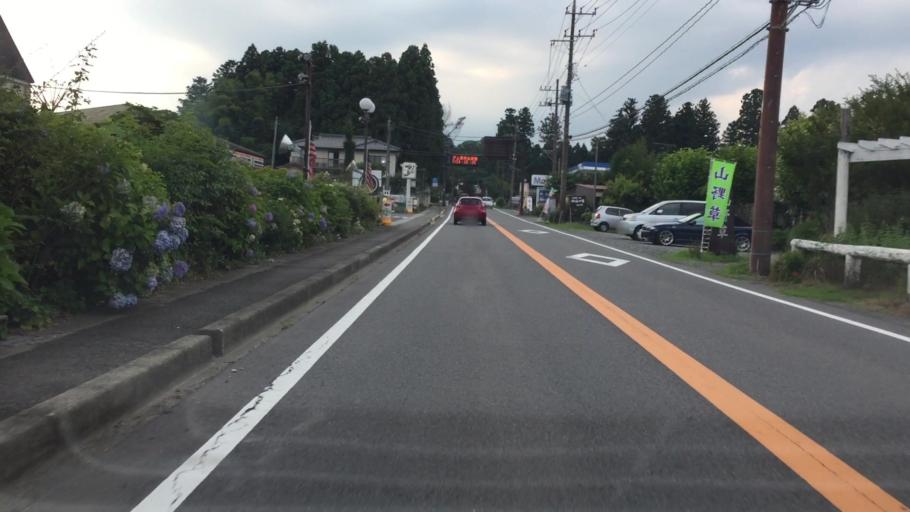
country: JP
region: Tochigi
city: Kuroiso
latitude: 37.0076
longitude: 140.0323
